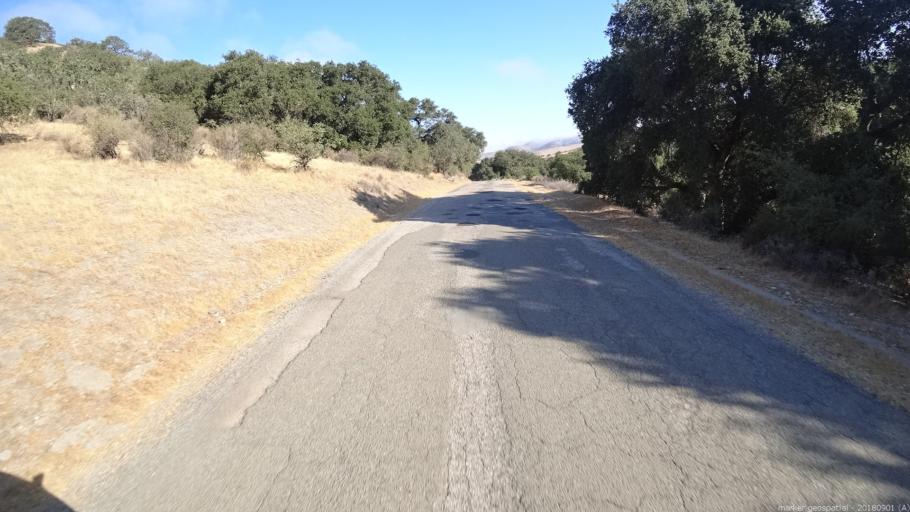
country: US
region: California
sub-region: Monterey County
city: Greenfield
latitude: 36.2331
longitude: -121.2832
